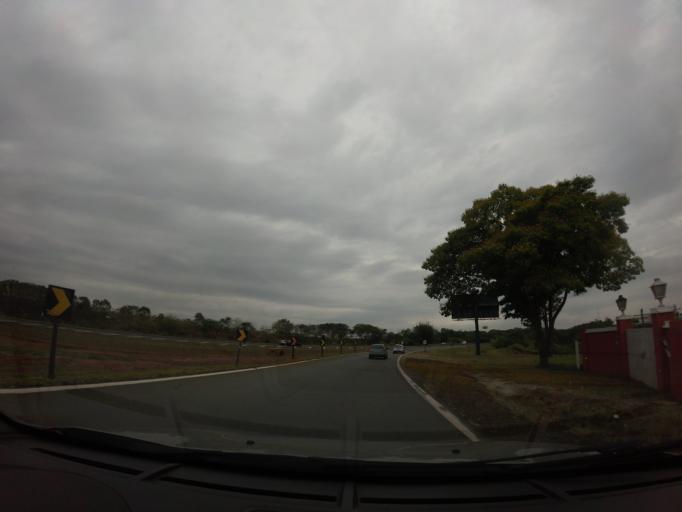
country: BR
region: Sao Paulo
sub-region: Piracicaba
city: Piracicaba
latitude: -22.7225
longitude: -47.6049
